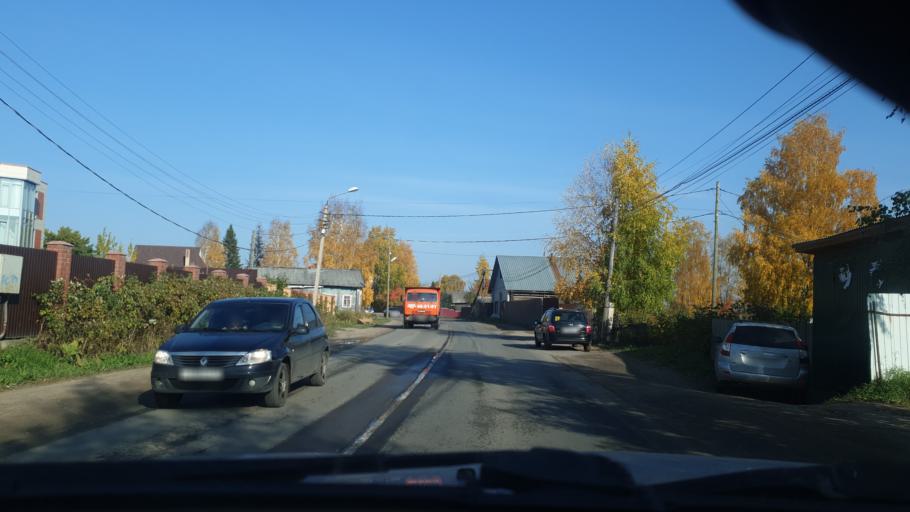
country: RU
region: Komi Republic
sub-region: Syktyvdinskiy Rayon
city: Syktyvkar
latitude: 61.6865
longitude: 50.8309
